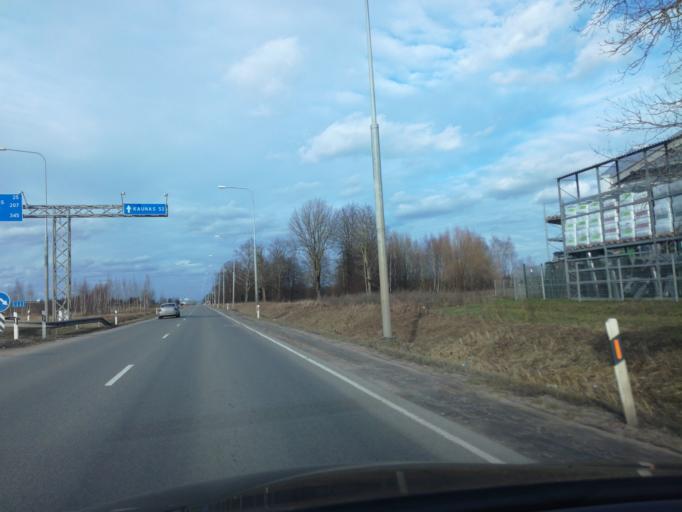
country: LT
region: Marijampoles apskritis
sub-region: Marijampole Municipality
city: Marijampole
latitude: 54.5818
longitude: 23.3776
